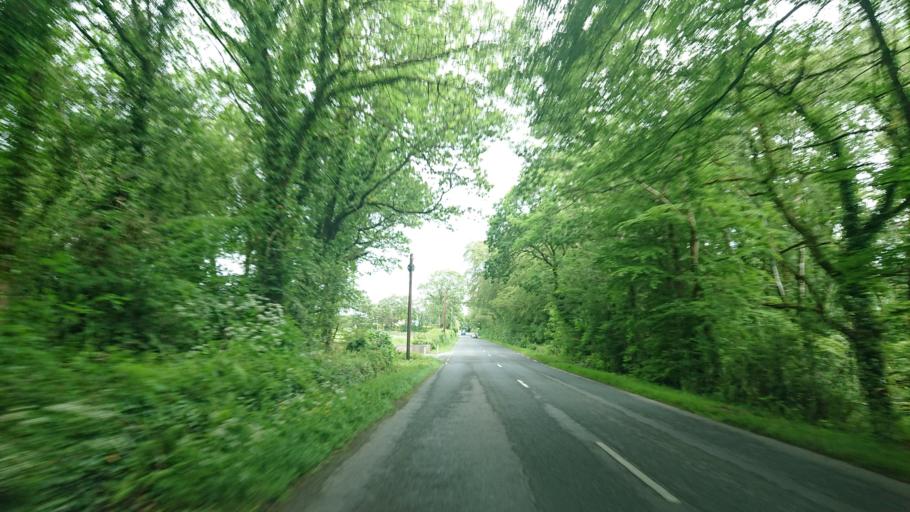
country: IE
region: Leinster
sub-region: Kilkenny
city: Graiguenamanagh
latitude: 52.4715
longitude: -6.9554
